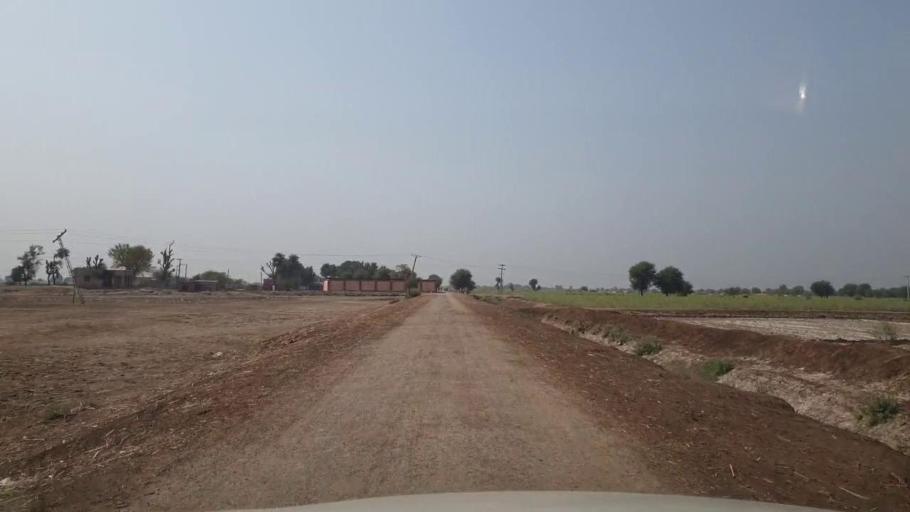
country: PK
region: Sindh
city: Chor
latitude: 25.4716
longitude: 69.6784
